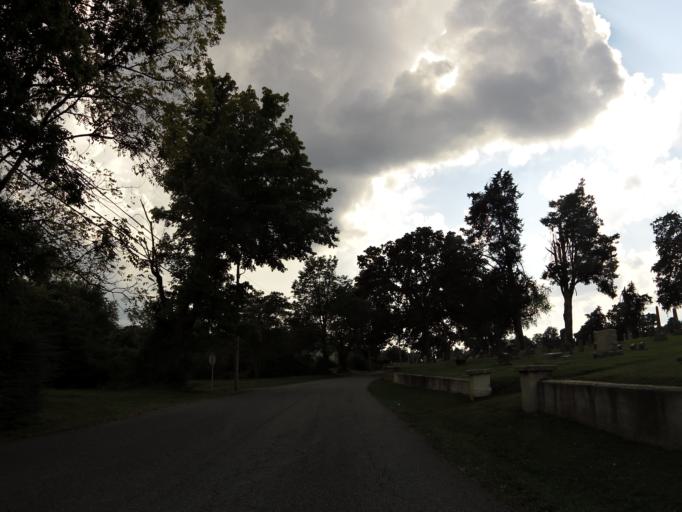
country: US
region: Tennessee
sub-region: Dickson County
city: Dickson
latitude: 36.0818
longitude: -87.3842
